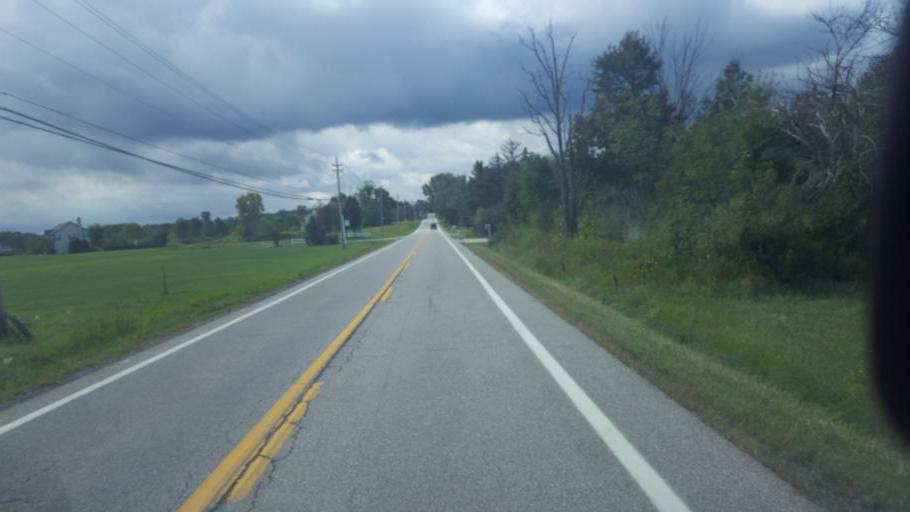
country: US
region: Ohio
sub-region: Geauga County
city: Chardon
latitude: 41.6130
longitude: -81.1357
